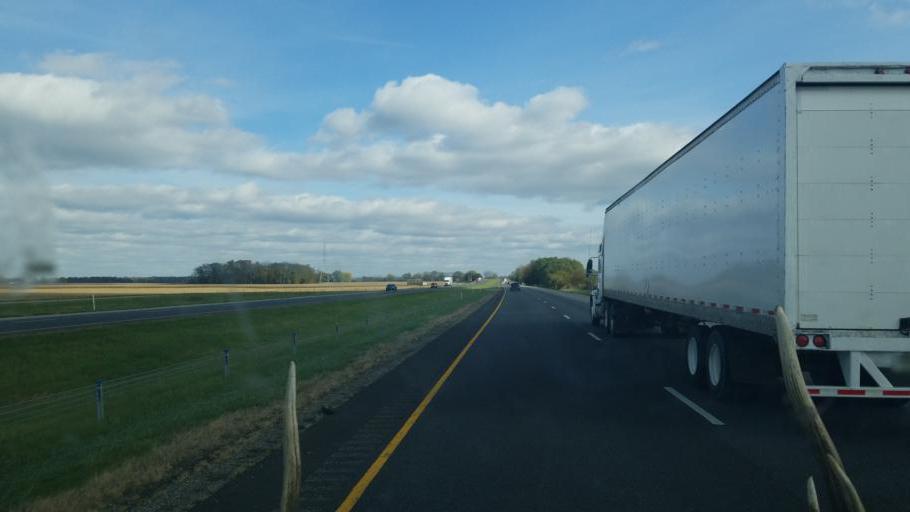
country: US
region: Indiana
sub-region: Wayne County
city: Cambridge City
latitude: 39.8527
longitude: -85.1187
